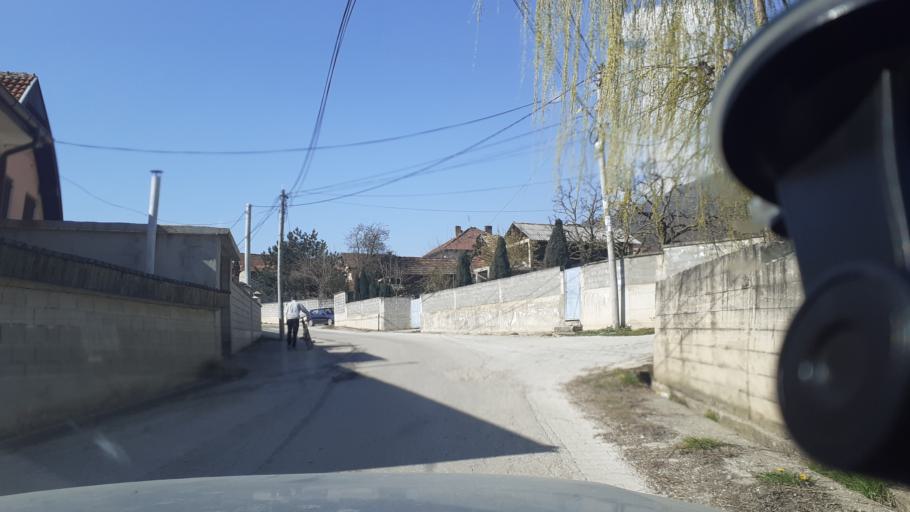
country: MK
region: Tearce
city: Slatino
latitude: 42.0707
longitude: 21.0414
